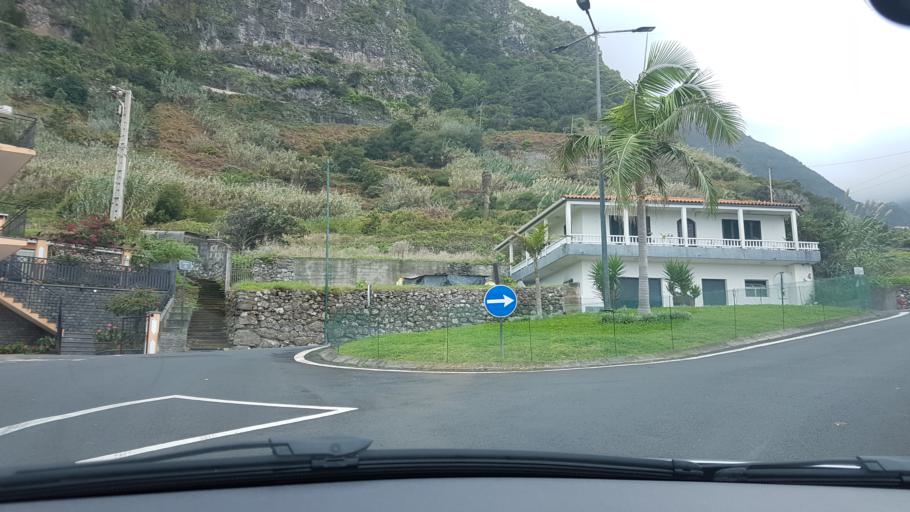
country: PT
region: Madeira
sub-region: Sao Vicente
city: Sao Vicente
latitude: 32.8267
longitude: -16.9850
